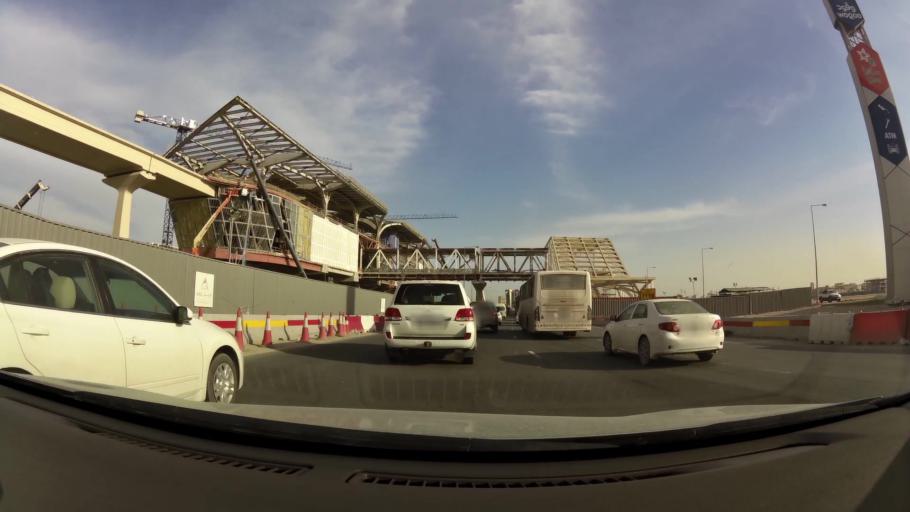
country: QA
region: Al Wakrah
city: Al Wakrah
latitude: 25.1945
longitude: 51.5948
